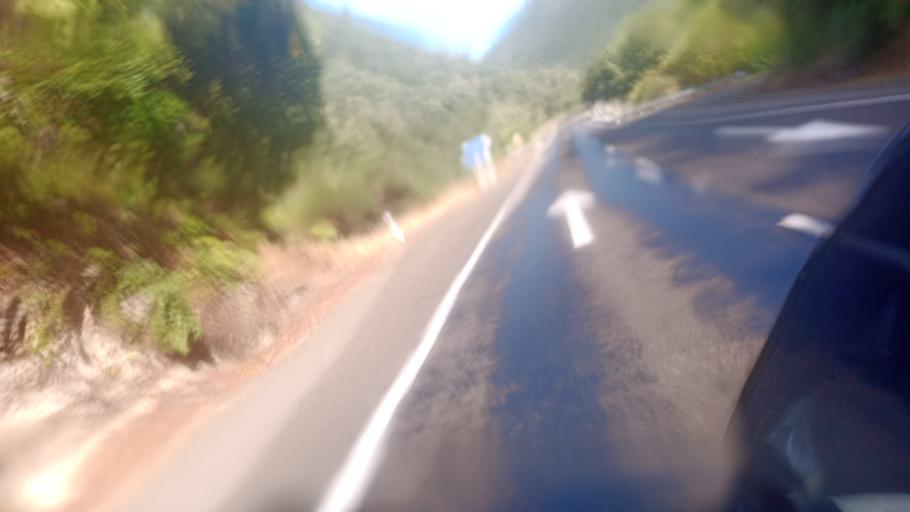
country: NZ
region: Bay of Plenty
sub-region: Opotiki District
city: Opotiki
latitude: -38.2921
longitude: 177.3857
